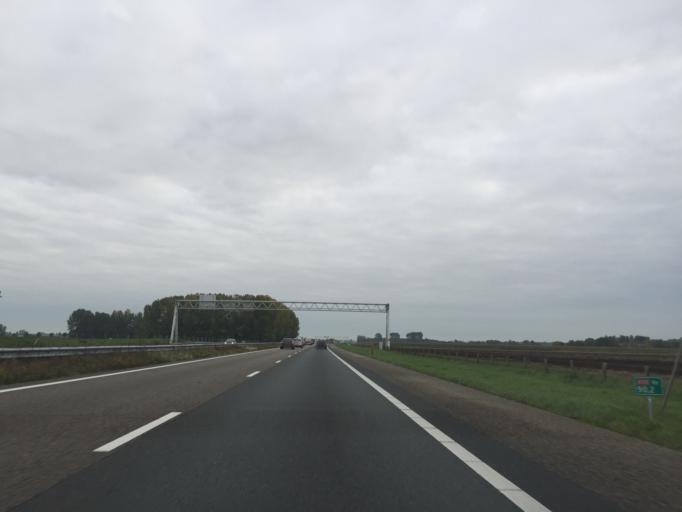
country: NL
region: North Brabant
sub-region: Gemeente Made en Drimmelen
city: Made
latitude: 51.6495
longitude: 4.7127
